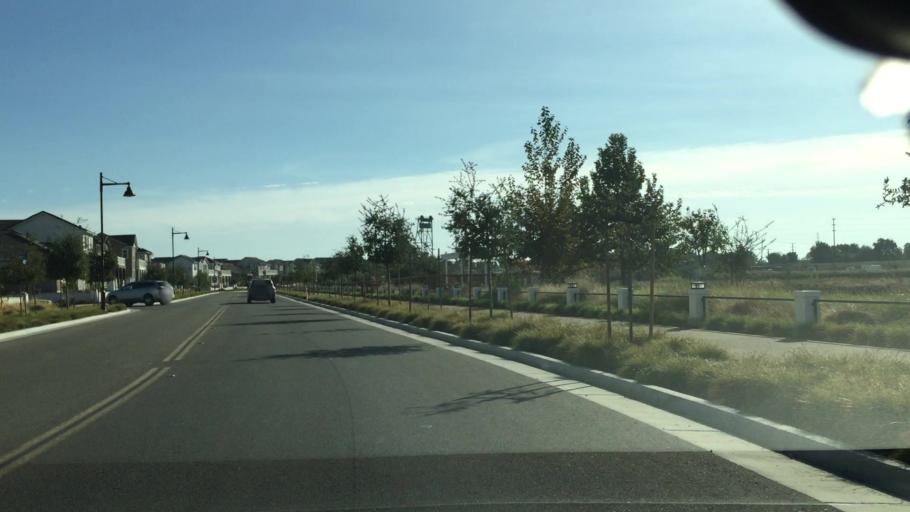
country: US
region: California
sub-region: San Joaquin County
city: Lathrop
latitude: 37.7899
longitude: -121.3146
